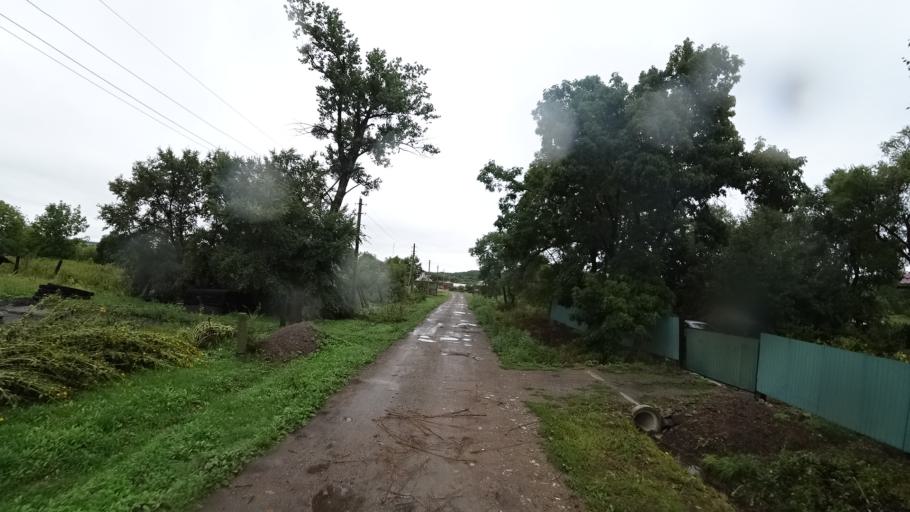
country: RU
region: Primorskiy
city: Monastyrishche
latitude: 44.2350
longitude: 132.4641
